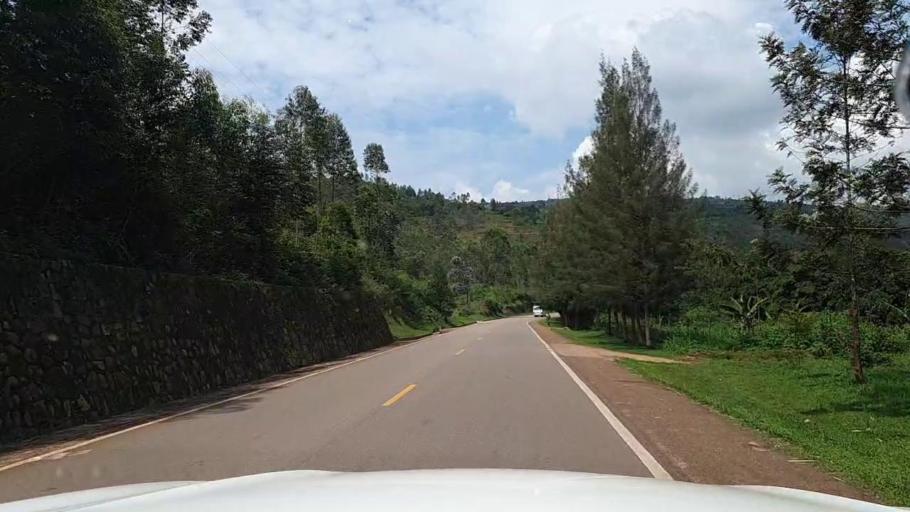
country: RW
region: Kigali
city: Kigali
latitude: -1.8427
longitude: 30.0882
